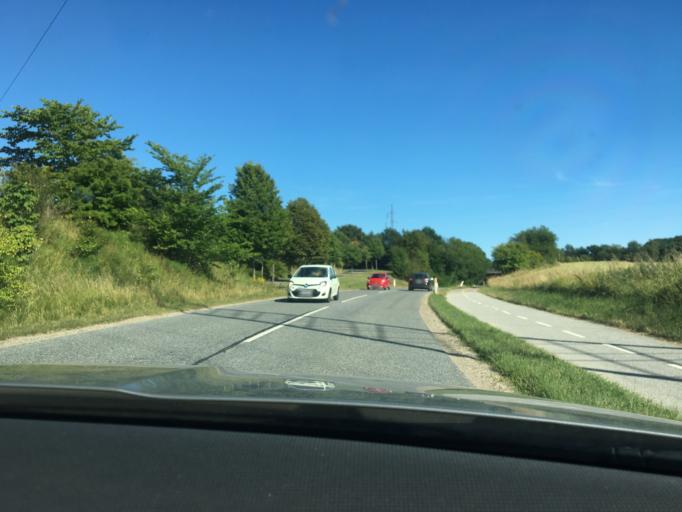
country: DK
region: Central Jutland
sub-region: Syddjurs Kommune
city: Hornslet
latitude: 56.3065
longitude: 10.3507
